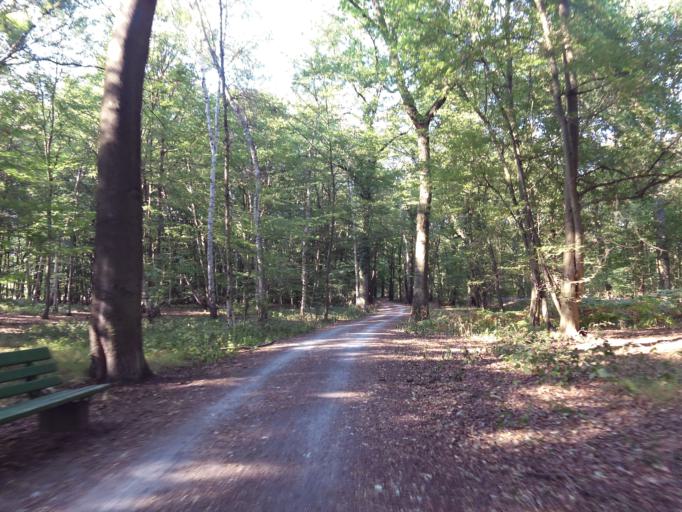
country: DE
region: Hesse
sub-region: Regierungsbezirk Darmstadt
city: Nauheim
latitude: 49.9712
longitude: 8.4571
